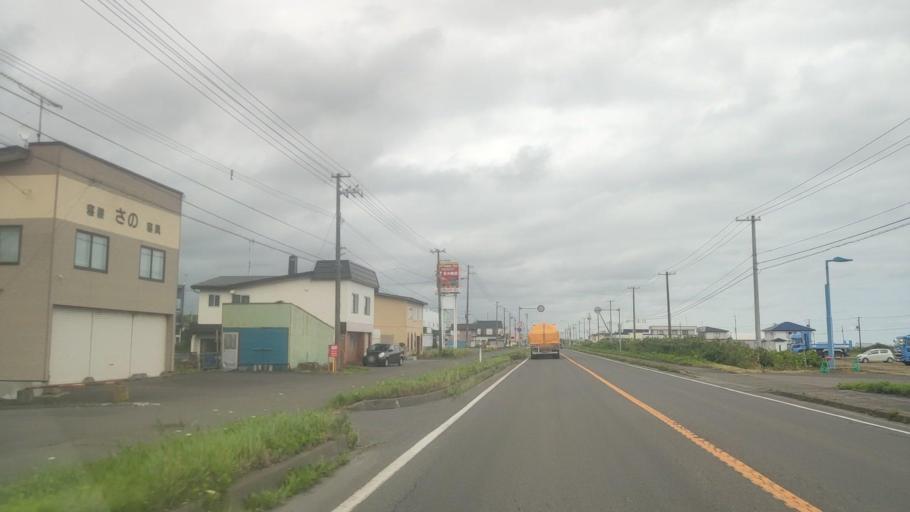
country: JP
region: Hokkaido
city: Shiraoi
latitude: 42.5125
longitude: 141.2945
